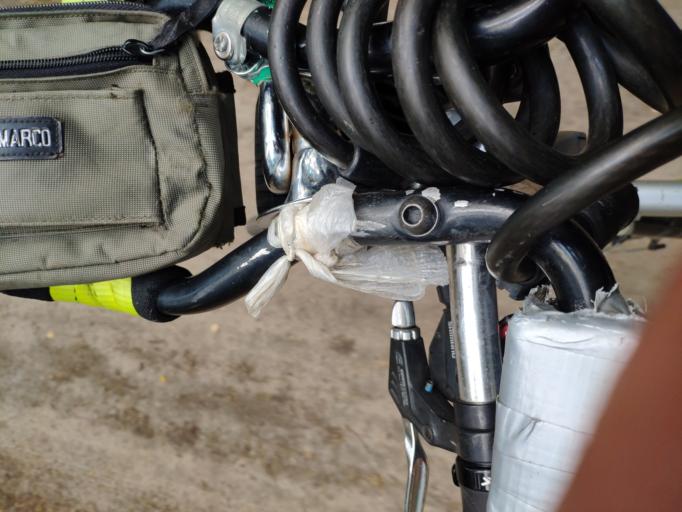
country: PL
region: Lubusz
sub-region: Zielona Gora
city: Zielona Gora
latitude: 51.9433
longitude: 15.5699
